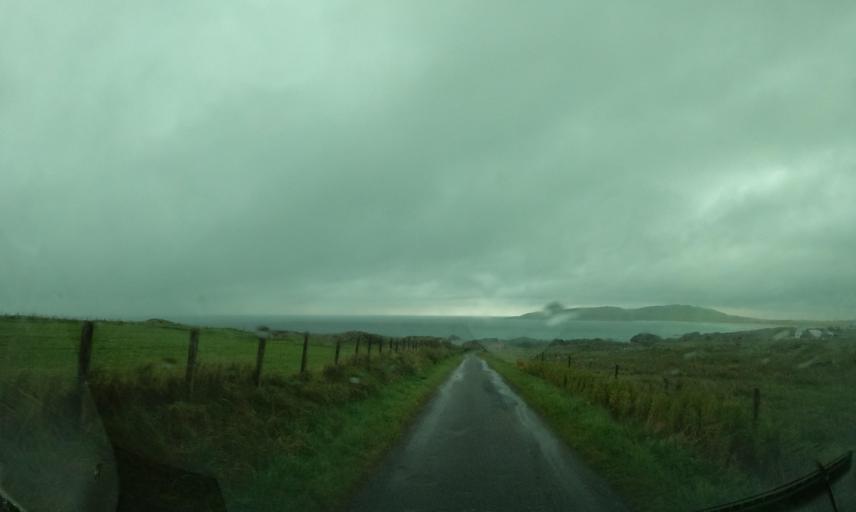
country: GB
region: Scotland
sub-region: Eilean Siar
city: Barra
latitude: 56.4515
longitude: -6.9358
